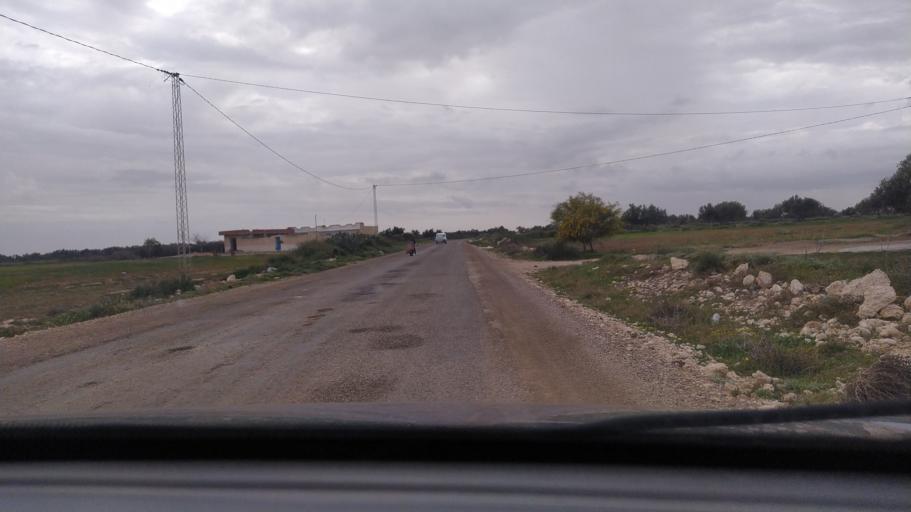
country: TN
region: Al Munastir
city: Sidi Bin Nur
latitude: 35.5067
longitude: 10.9610
